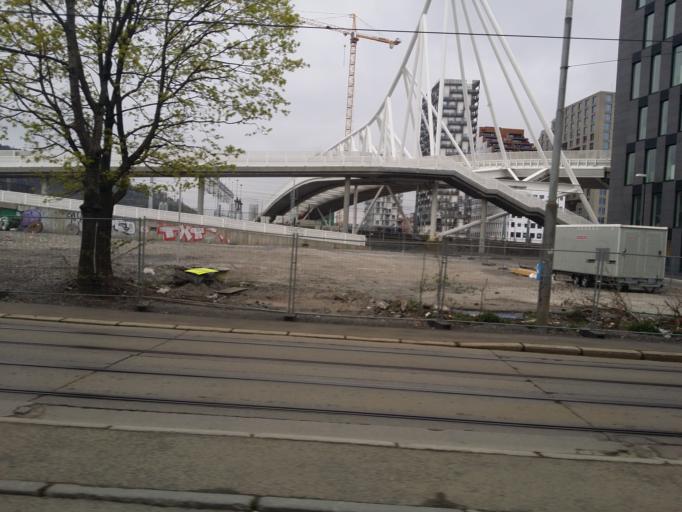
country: NO
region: Oslo
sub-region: Oslo
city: Oslo
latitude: 59.9098
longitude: 10.7644
